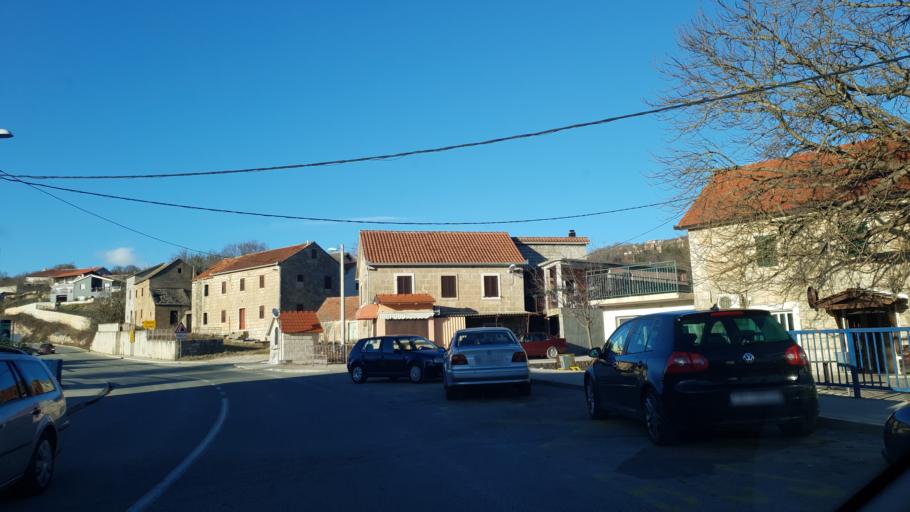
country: HR
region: Splitsko-Dalmatinska
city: Gala
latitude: 43.7298
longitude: 16.6956
